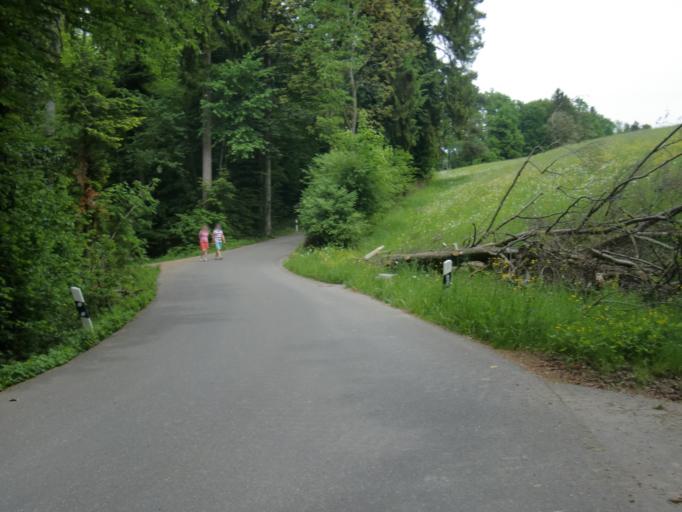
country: CH
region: Zurich
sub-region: Bezirk Hinwil
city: Hadlikon
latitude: 47.2891
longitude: 8.8630
